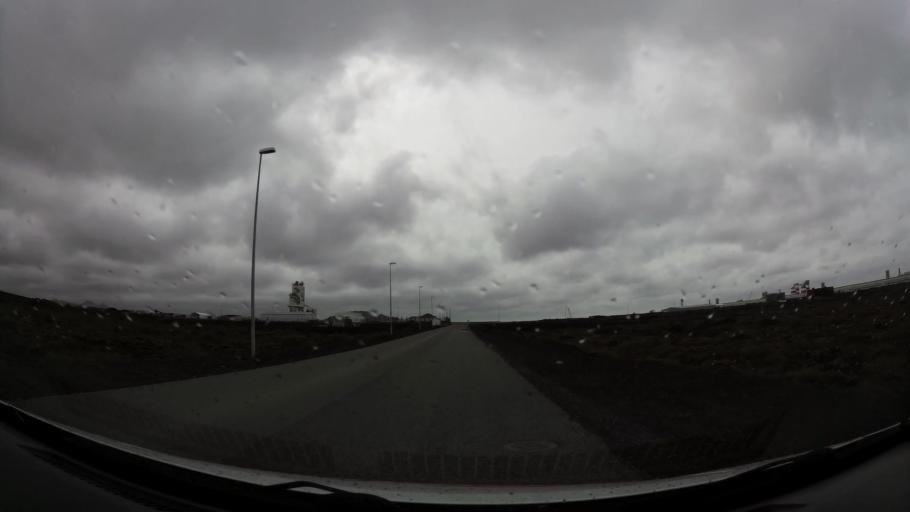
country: IS
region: Capital Region
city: Alftanes
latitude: 64.0415
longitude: -22.0048
